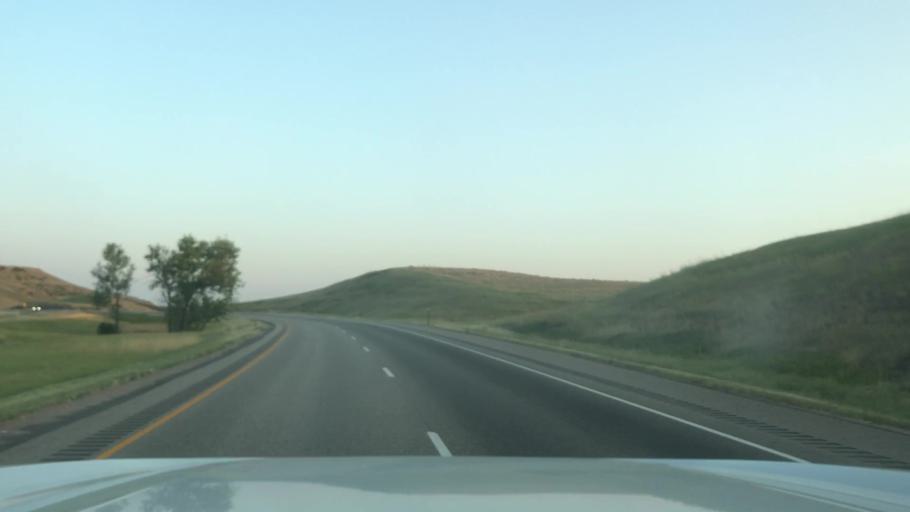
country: US
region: Wyoming
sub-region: Sheridan County
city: Sheridan
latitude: 44.7050
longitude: -106.9110
